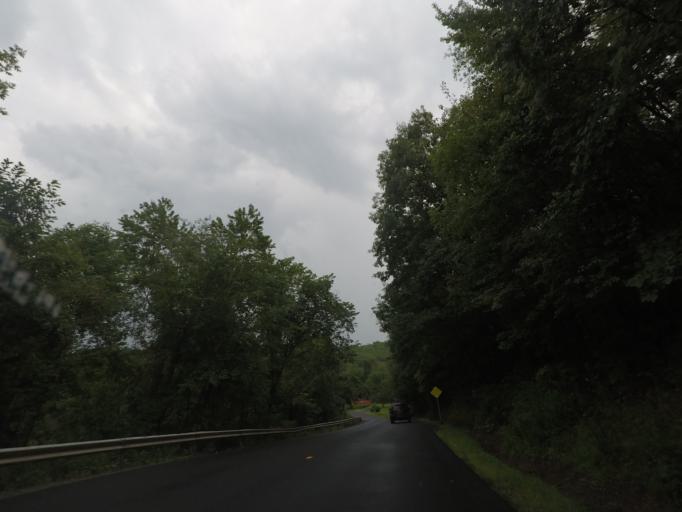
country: US
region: New York
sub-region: Rensselaer County
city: Poestenkill
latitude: 42.6889
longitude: -73.5511
